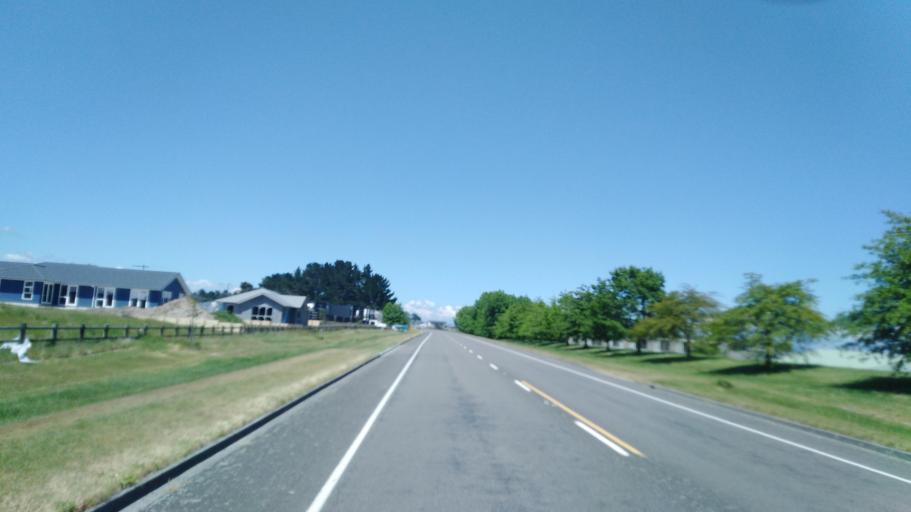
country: NZ
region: Waikato
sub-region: Taupo District
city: Taupo
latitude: -38.7306
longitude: 176.0736
